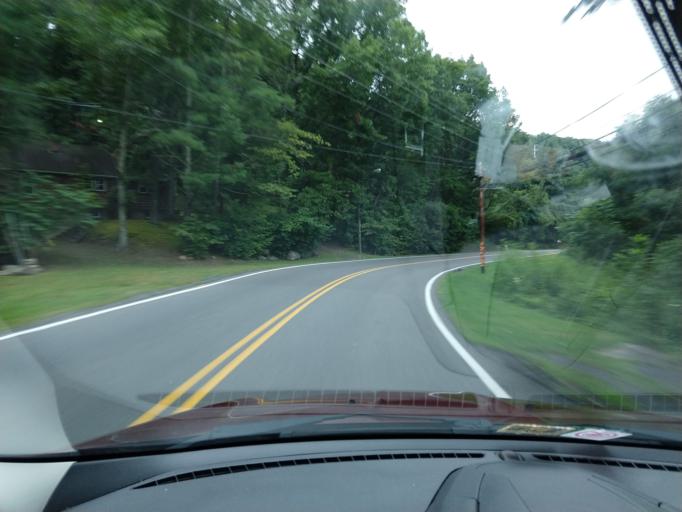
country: US
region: Virginia
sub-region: City of Covington
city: Fairlawn
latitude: 37.7712
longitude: -79.9851
